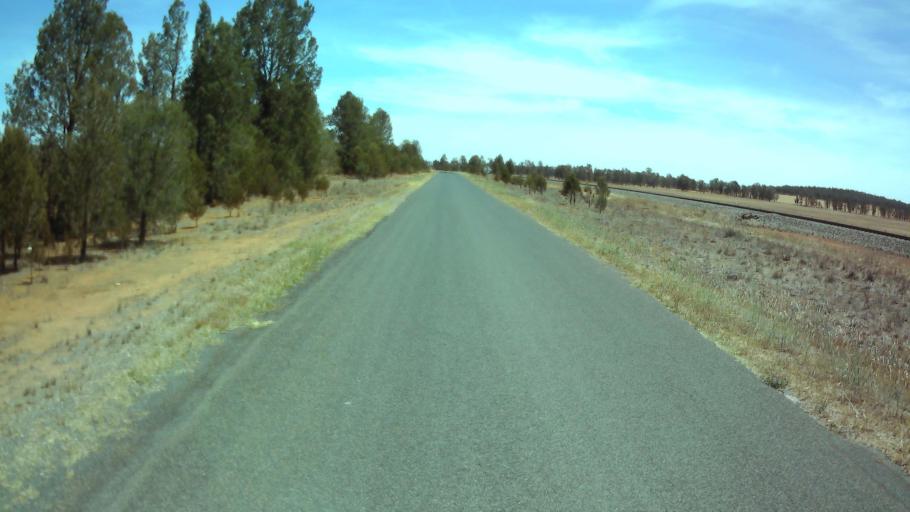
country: AU
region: New South Wales
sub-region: Weddin
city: Grenfell
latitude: -33.7748
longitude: 147.7553
